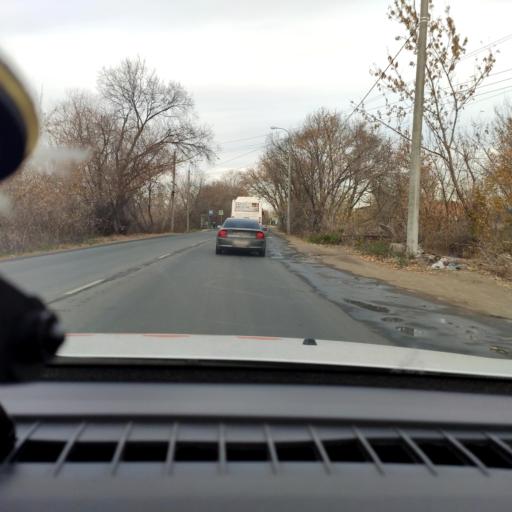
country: RU
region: Samara
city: Rozhdestveno
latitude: 53.1441
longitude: 50.0319
